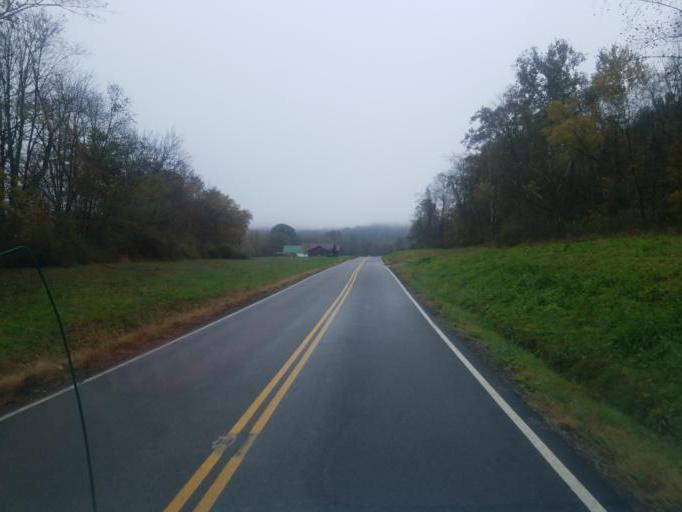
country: US
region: Ohio
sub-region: Morgan County
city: McConnelsville
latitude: 39.6093
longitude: -81.8232
